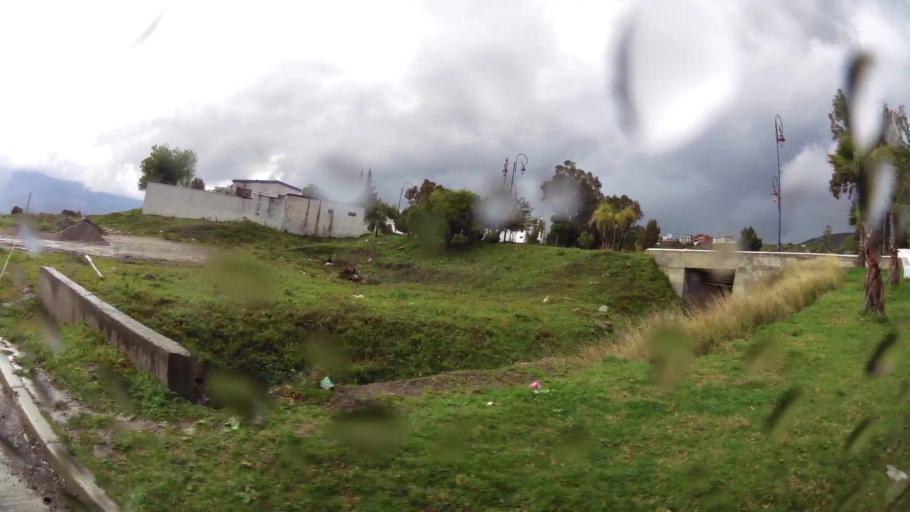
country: MA
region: Tanger-Tetouan
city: Chefchaouene
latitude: 35.1738
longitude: -5.2787
